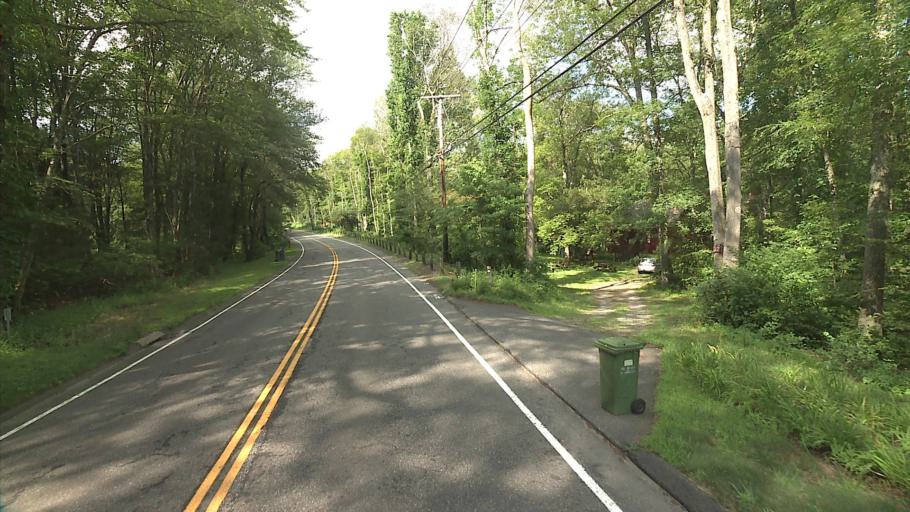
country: US
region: Connecticut
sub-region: Middlesex County
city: Chester Center
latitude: 41.3914
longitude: -72.5047
